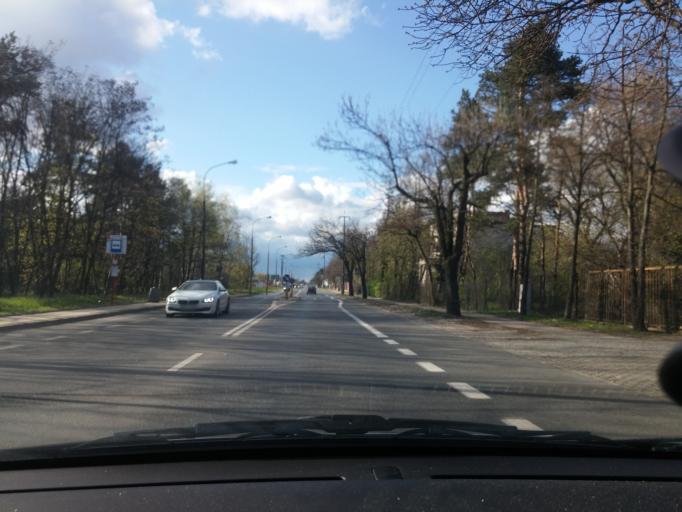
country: PL
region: Masovian Voivodeship
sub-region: Warszawa
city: Wawer
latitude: 52.1879
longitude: 21.1855
